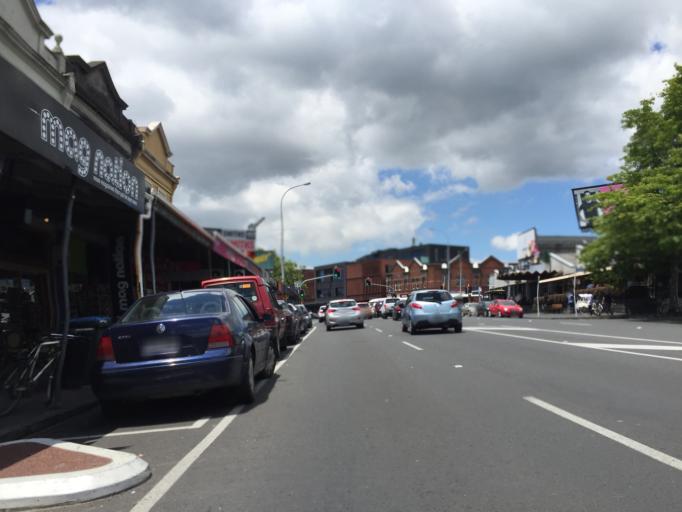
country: NZ
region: Auckland
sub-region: Auckland
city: Auckland
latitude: -36.8555
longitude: 174.7464
